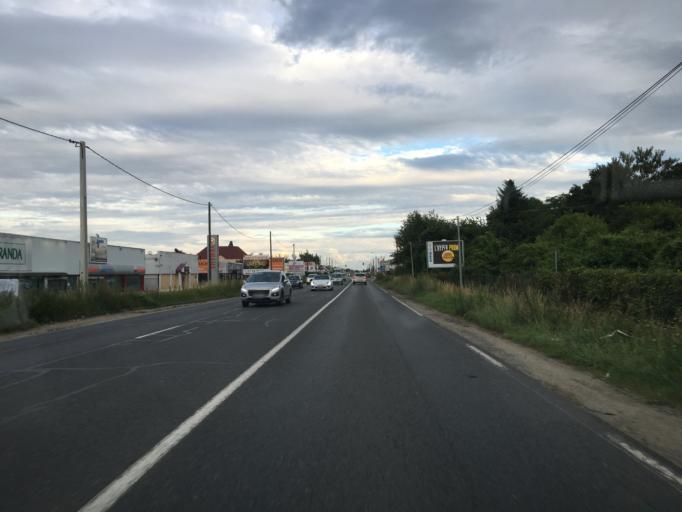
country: FR
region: Ile-de-France
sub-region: Departement de Seine-et-Marne
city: Servon
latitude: 48.7136
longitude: 2.5775
